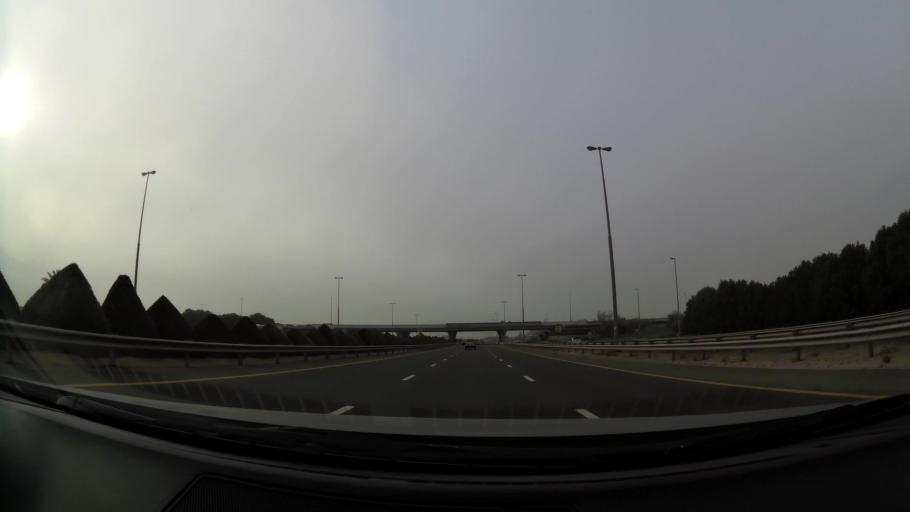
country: AE
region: Dubai
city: Dubai
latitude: 25.1764
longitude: 55.3192
